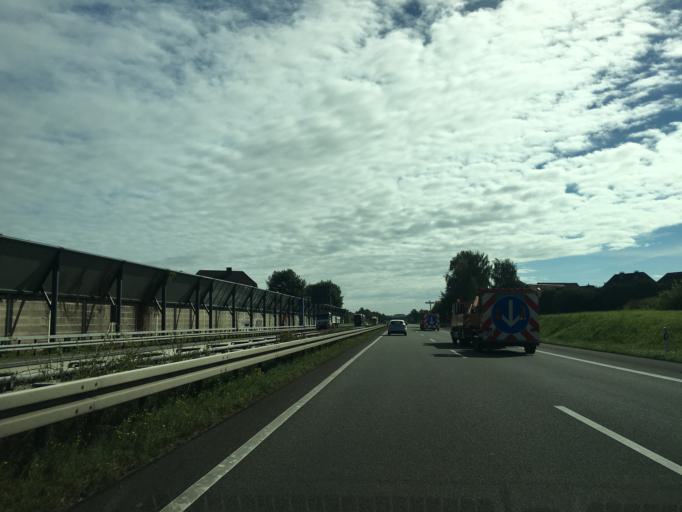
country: DE
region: Lower Saxony
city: Melle
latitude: 52.1937
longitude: 8.3454
